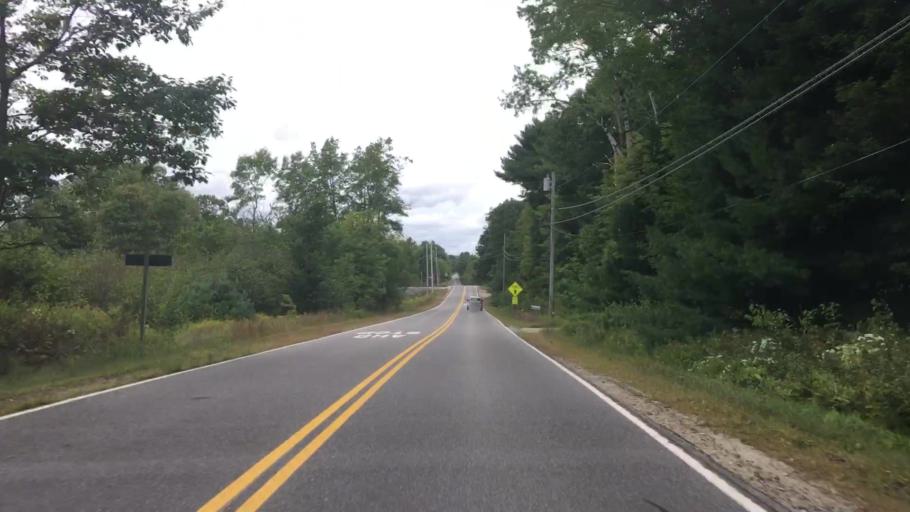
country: US
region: Maine
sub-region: Cumberland County
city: Yarmouth
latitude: 43.8582
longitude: -70.2172
